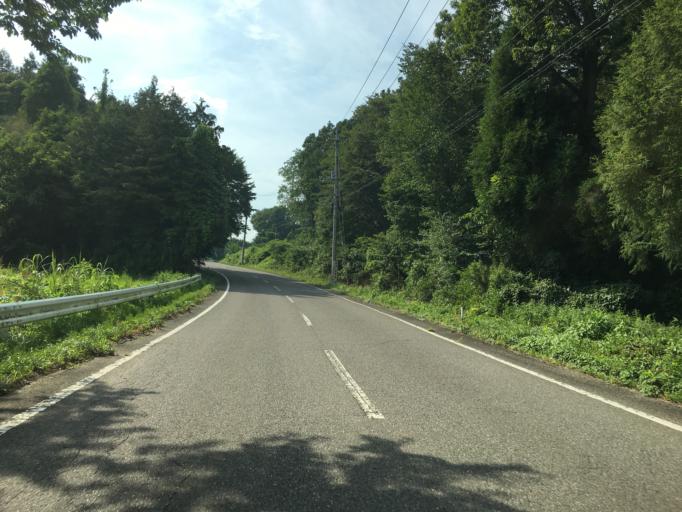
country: JP
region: Fukushima
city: Sukagawa
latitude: 37.3296
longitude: 140.4305
